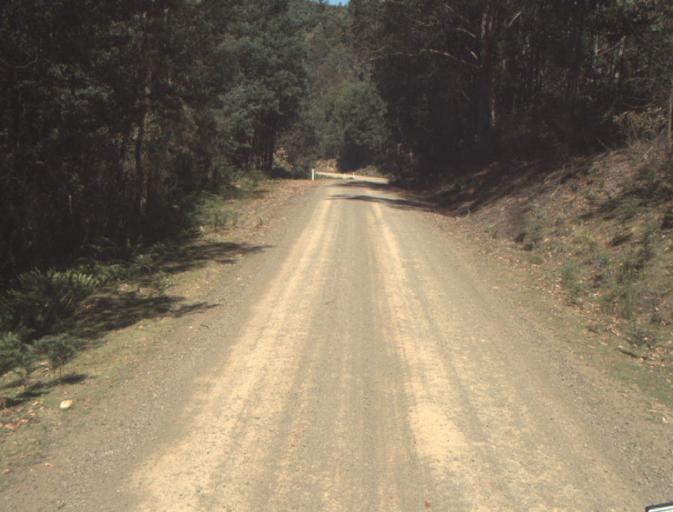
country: AU
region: Tasmania
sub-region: Dorset
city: Scottsdale
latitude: -41.3782
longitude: 147.4790
